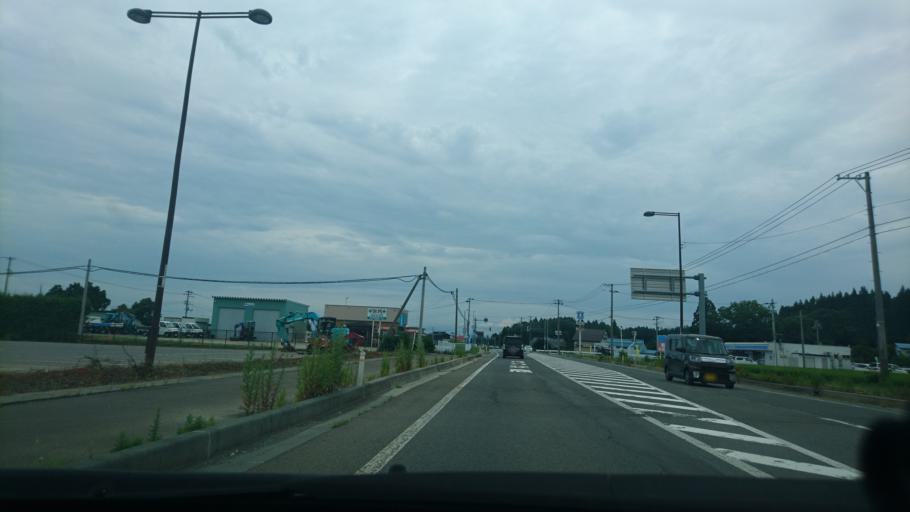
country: JP
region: Akita
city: Yokotemachi
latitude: 39.3799
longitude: 140.5681
